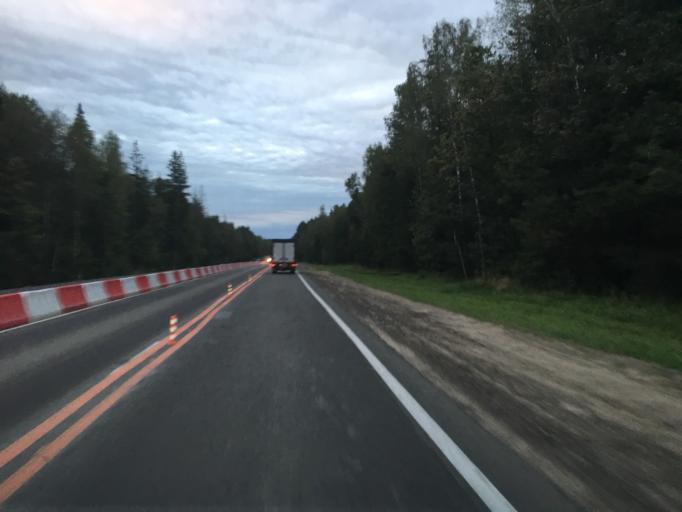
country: RU
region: Kaluga
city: Detchino
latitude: 54.6982
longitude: 36.2939
